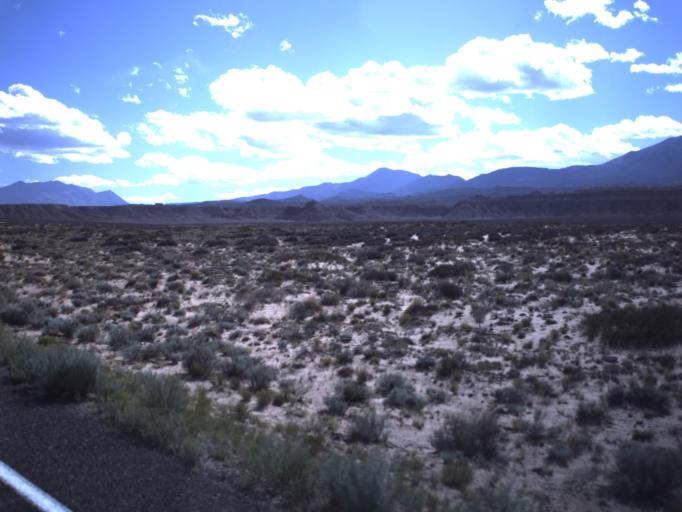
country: US
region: Utah
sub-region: Wayne County
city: Loa
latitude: 38.1707
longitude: -110.6240
